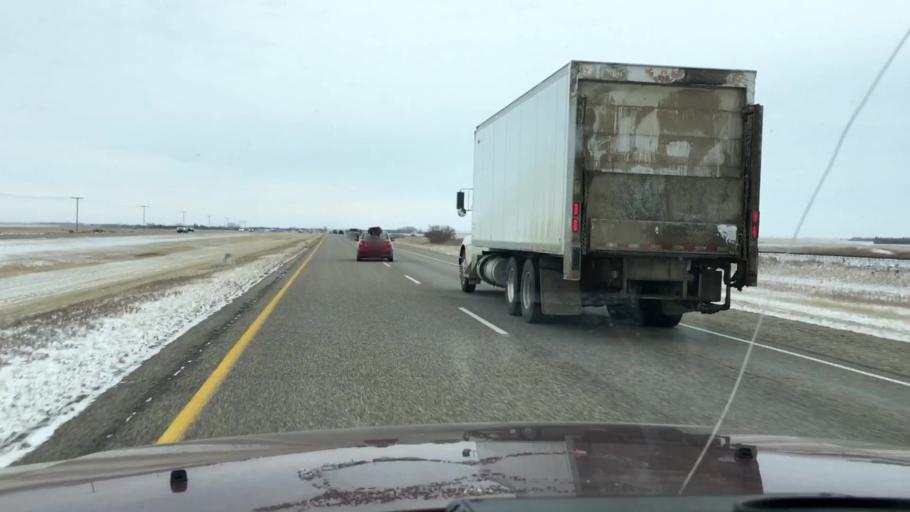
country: CA
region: Saskatchewan
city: Watrous
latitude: 51.1783
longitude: -105.9374
